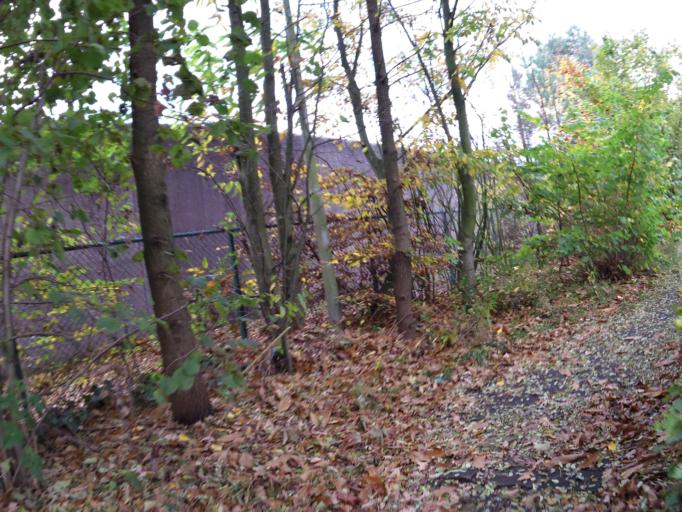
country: NL
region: North Brabant
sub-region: Gemeente Vught
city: Vught
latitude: 51.6620
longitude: 5.2540
